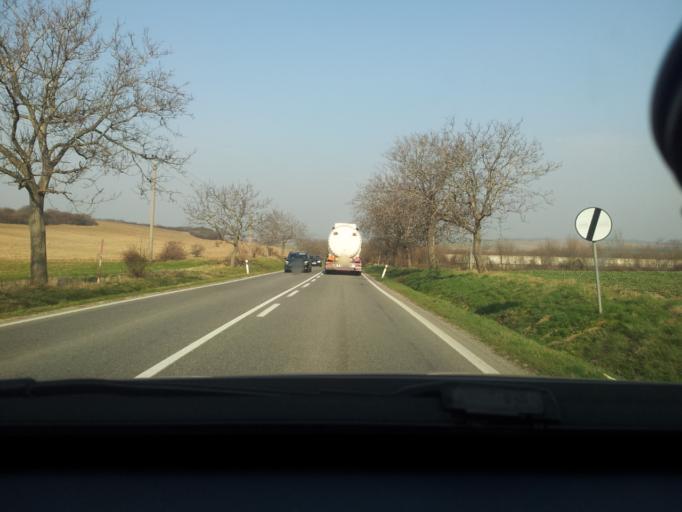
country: SK
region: Nitriansky
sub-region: Okres Nitra
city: Nitra
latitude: 48.3540
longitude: 17.9438
